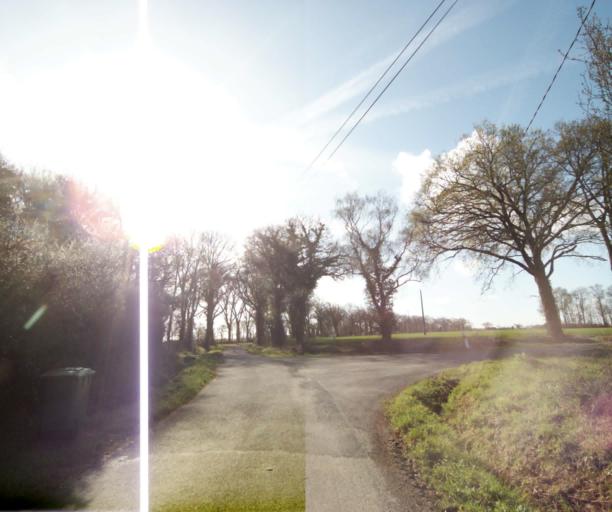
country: FR
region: Pays de la Loire
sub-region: Departement de la Loire-Atlantique
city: Bouvron
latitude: 47.3990
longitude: -1.8474
